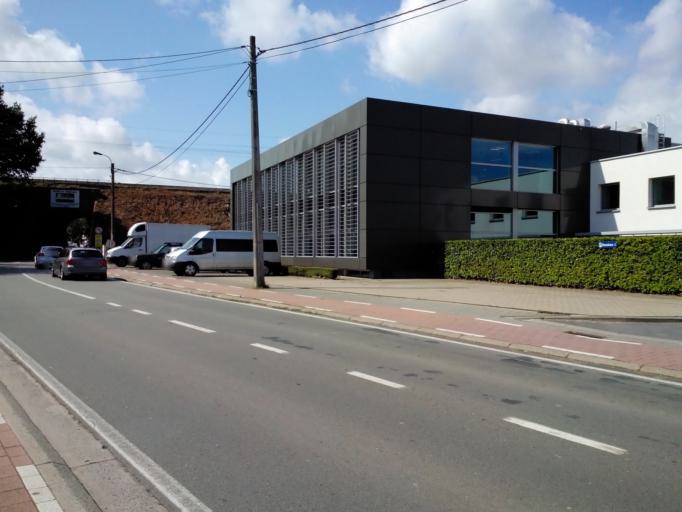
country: BE
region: Flanders
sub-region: Provincie Vlaams-Brabant
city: Asse
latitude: 50.9131
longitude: 4.2070
